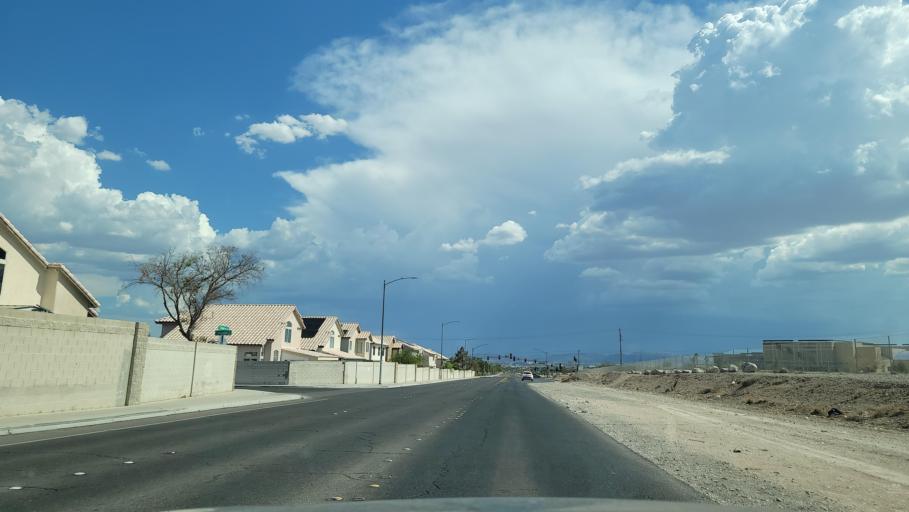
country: US
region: Nevada
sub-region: Clark County
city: Spring Valley
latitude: 36.1279
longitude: -115.2700
